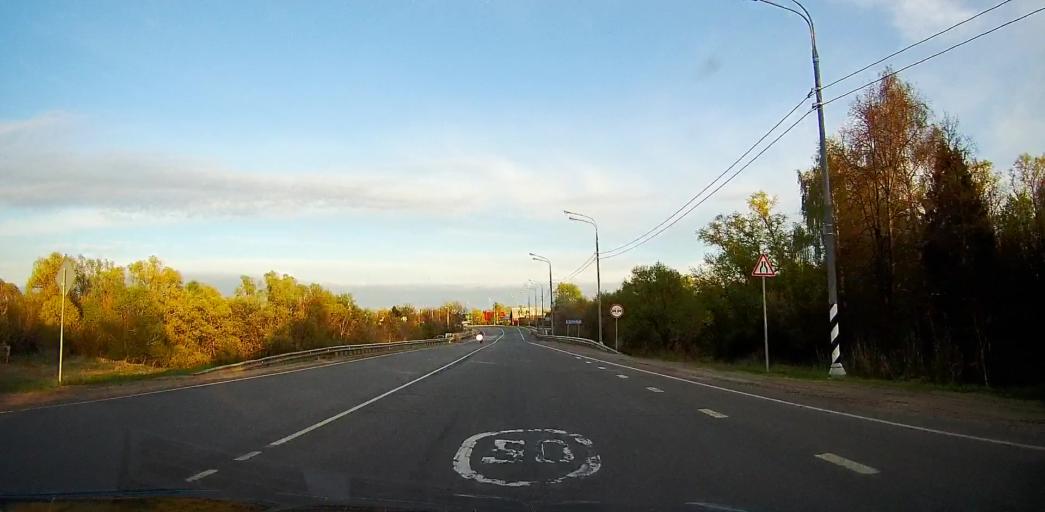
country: RU
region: Moskovskaya
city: Troitskoye
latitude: 55.2274
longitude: 38.5584
